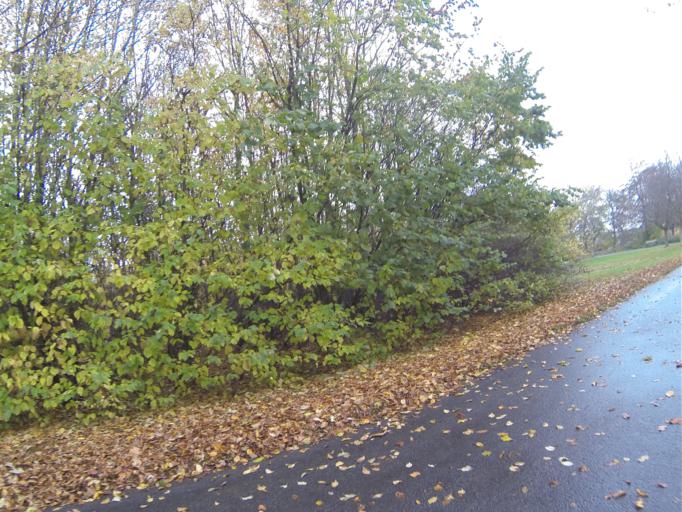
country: SE
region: Skane
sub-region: Eslovs Kommun
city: Eslov
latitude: 55.7226
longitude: 13.3473
